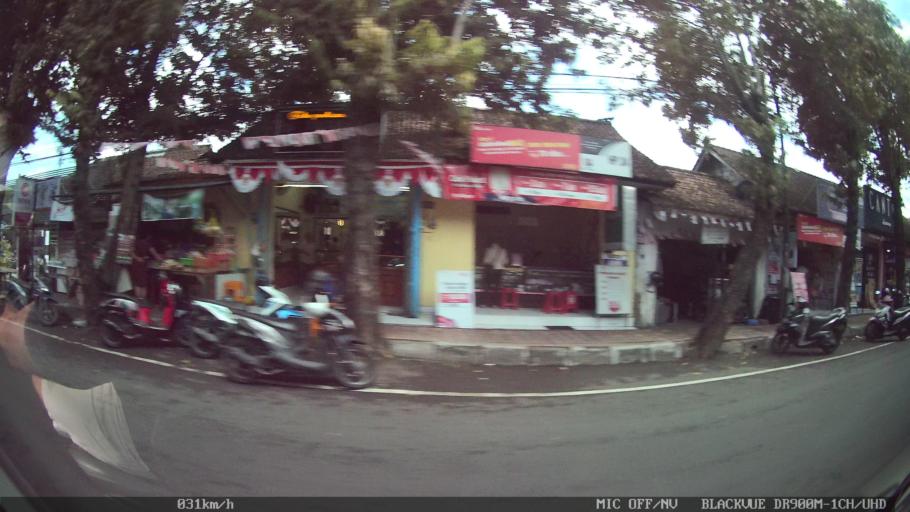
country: ID
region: Bali
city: Banjar Pasekan
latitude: -8.5931
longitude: 115.2825
